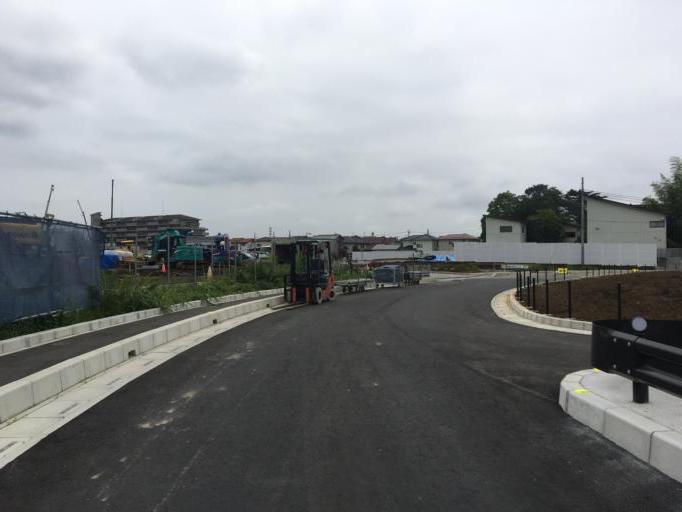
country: JP
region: Saitama
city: Ageoshimo
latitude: 35.9644
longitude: 139.5982
